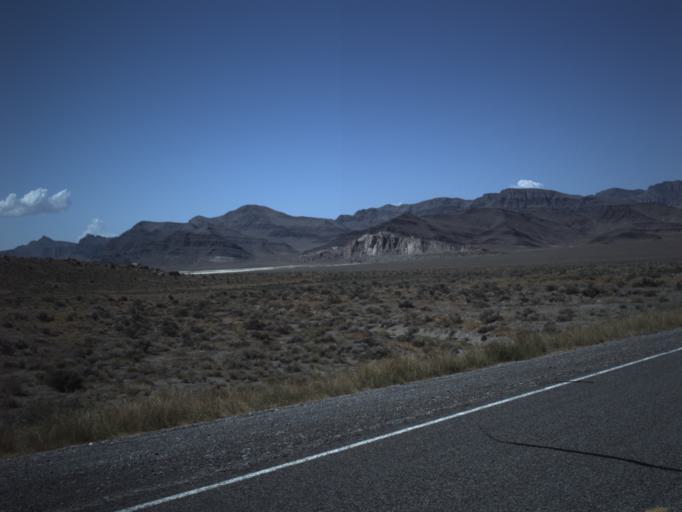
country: US
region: Utah
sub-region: Beaver County
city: Milford
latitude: 39.0246
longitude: -113.3571
